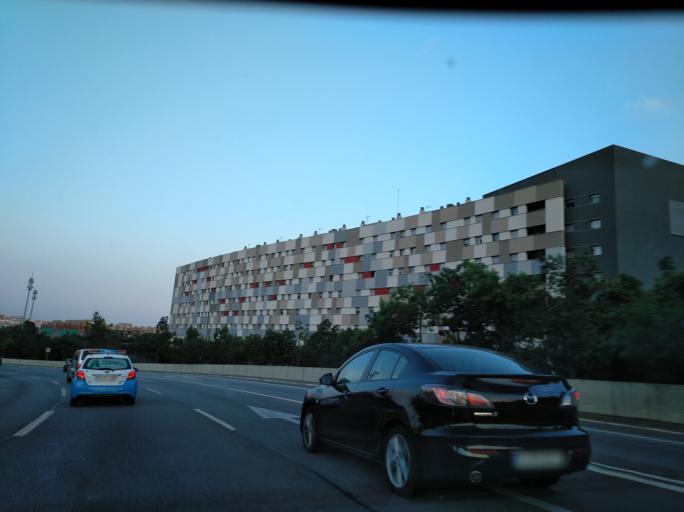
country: ES
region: Catalonia
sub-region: Provincia de Barcelona
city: Sant Andreu de Palomar
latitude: 41.4468
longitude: 2.1923
